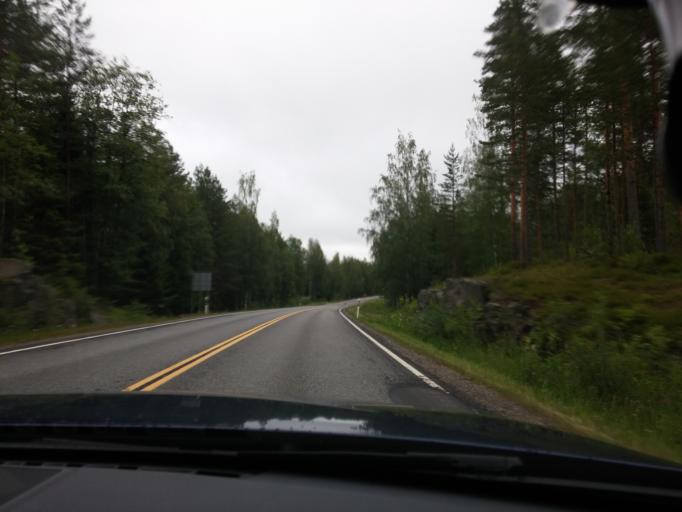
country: FI
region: Pirkanmaa
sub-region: Ylae-Pirkanmaa
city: Vilppula
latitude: 61.9511
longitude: 24.5472
